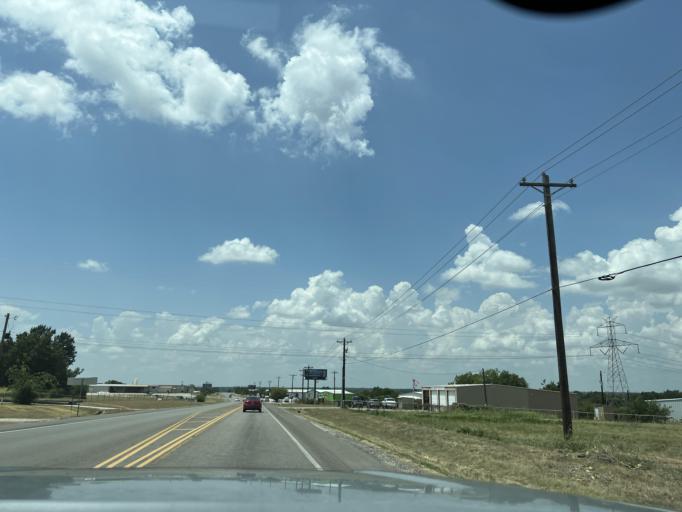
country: US
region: Texas
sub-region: Parker County
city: Weatherford
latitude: 32.8307
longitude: -97.7671
